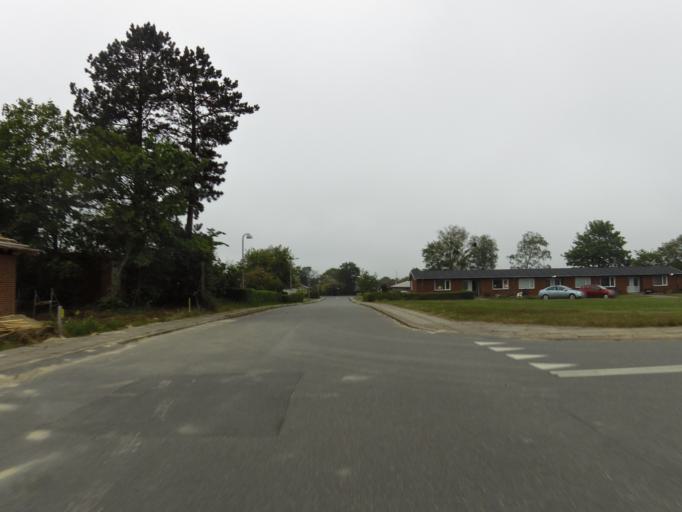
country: DK
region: South Denmark
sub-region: Esbjerg Kommune
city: Ribe
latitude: 55.3278
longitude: 8.7882
